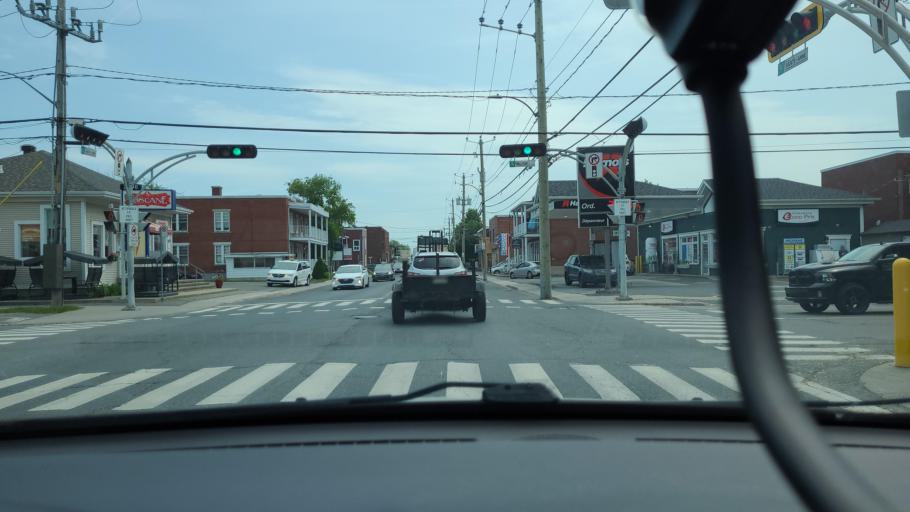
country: CA
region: Quebec
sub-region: Monteregie
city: Saint-Hyacinthe
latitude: 45.6308
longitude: -72.9560
